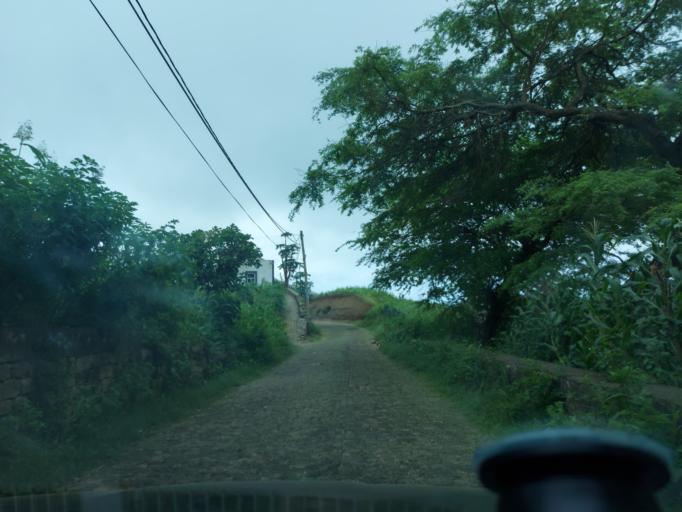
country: CV
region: Brava
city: Vila Nova Sintra
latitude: 14.8554
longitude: -24.7196
